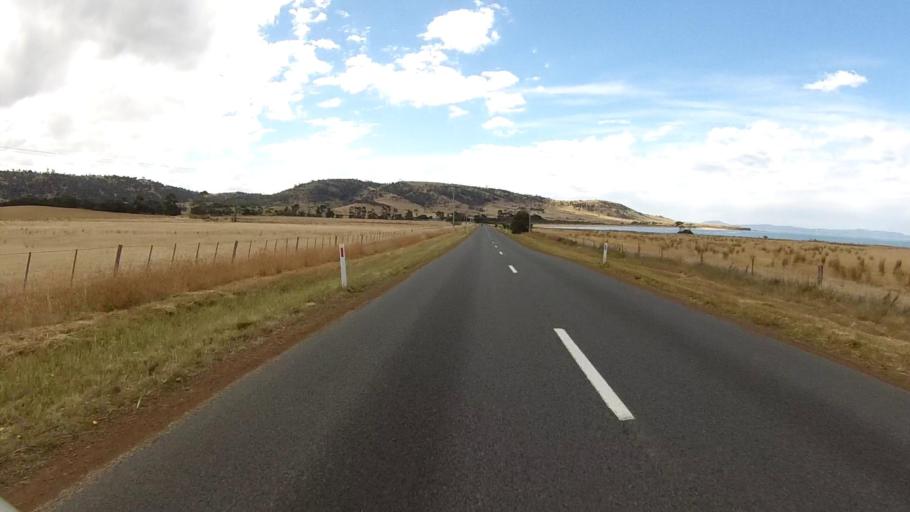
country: AU
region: Tasmania
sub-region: Sorell
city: Sorell
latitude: -42.2086
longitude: 148.0403
